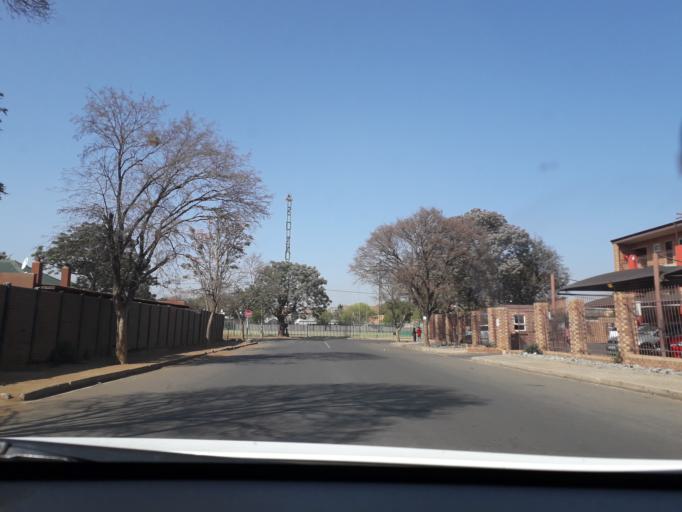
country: ZA
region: Gauteng
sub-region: City of Johannesburg Metropolitan Municipality
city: Modderfontein
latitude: -26.1017
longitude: 28.2368
